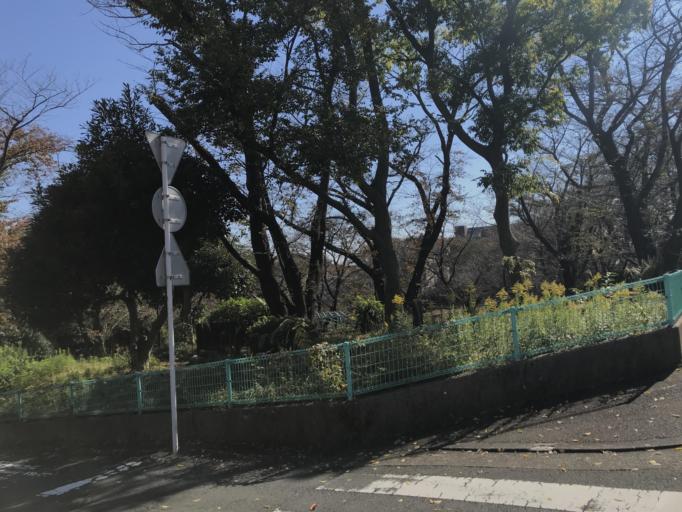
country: JP
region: Tokyo
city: Chofugaoka
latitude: 35.5812
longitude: 139.5794
